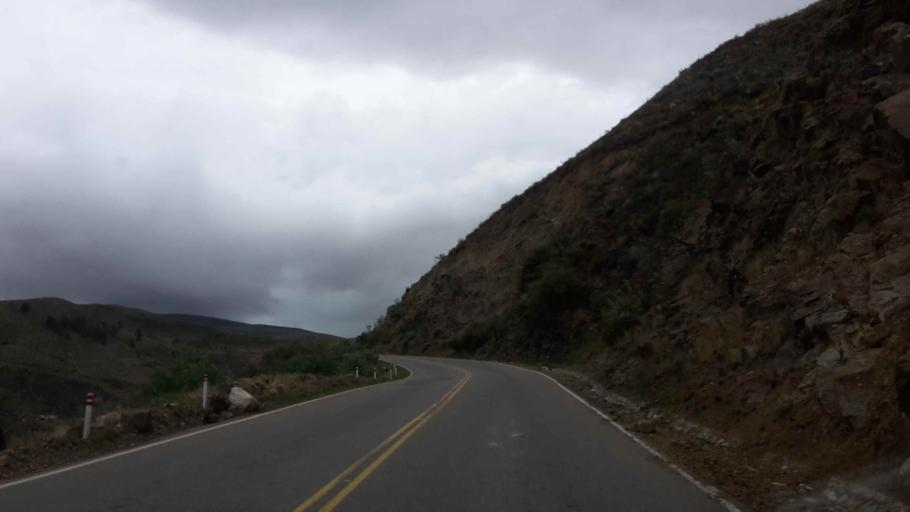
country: BO
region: Cochabamba
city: Punata
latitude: -17.4978
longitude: -65.7947
